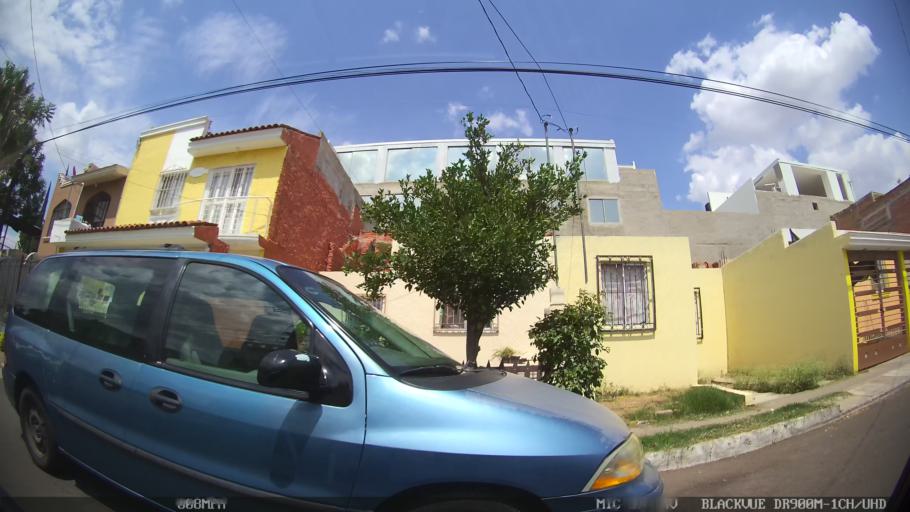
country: MX
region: Jalisco
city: Tonala
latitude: 20.6238
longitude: -103.2509
